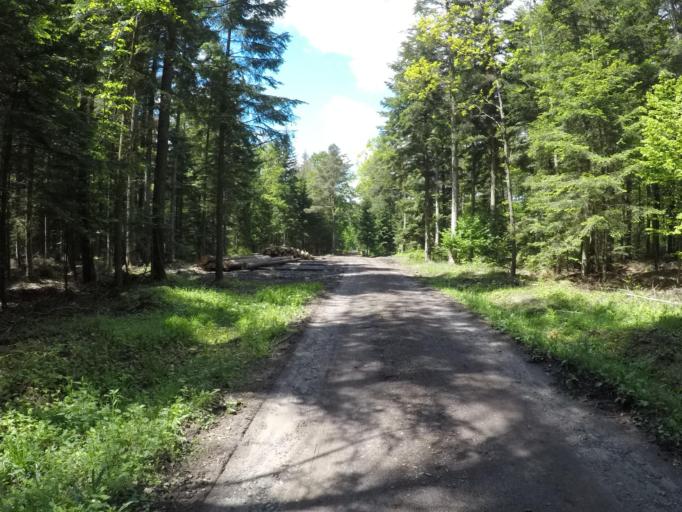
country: PL
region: Swietokrzyskie
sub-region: Powiat kielecki
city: Kostomloty Pierwsze
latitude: 50.9207
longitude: 20.6330
